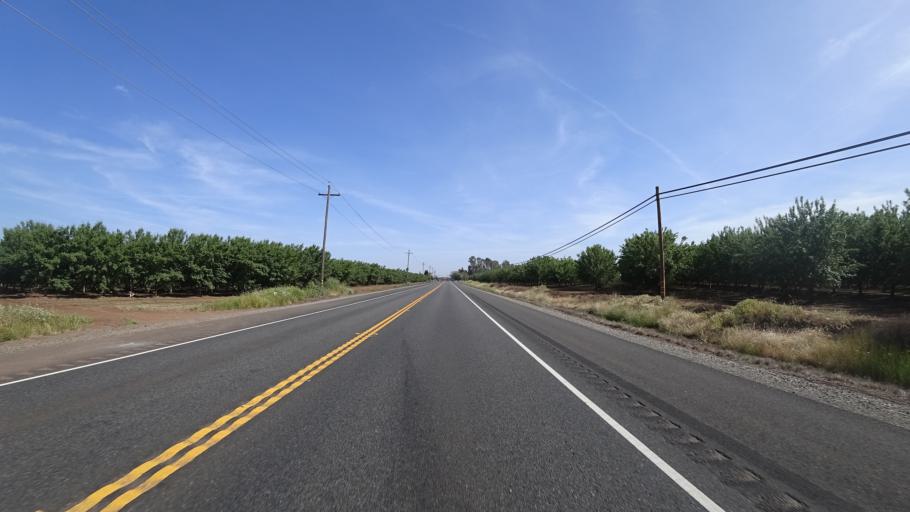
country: US
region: California
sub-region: Butte County
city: Chico
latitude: 39.8020
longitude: -121.9062
